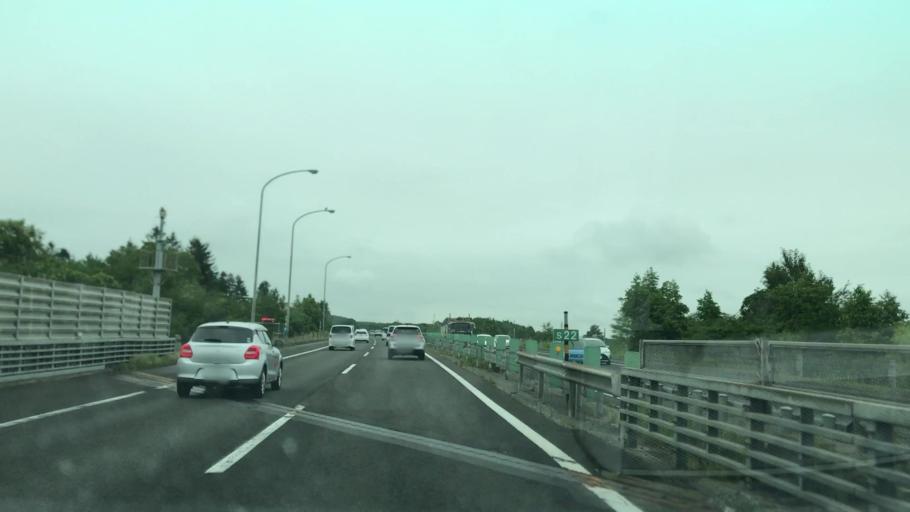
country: JP
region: Hokkaido
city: Kitahiroshima
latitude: 42.9093
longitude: 141.5502
